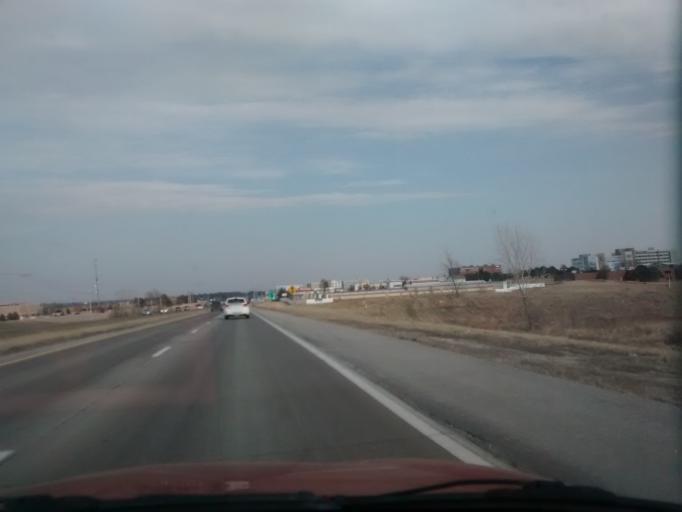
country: US
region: Nebraska
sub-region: Sarpy County
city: Papillion
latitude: 41.1399
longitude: -96.0486
